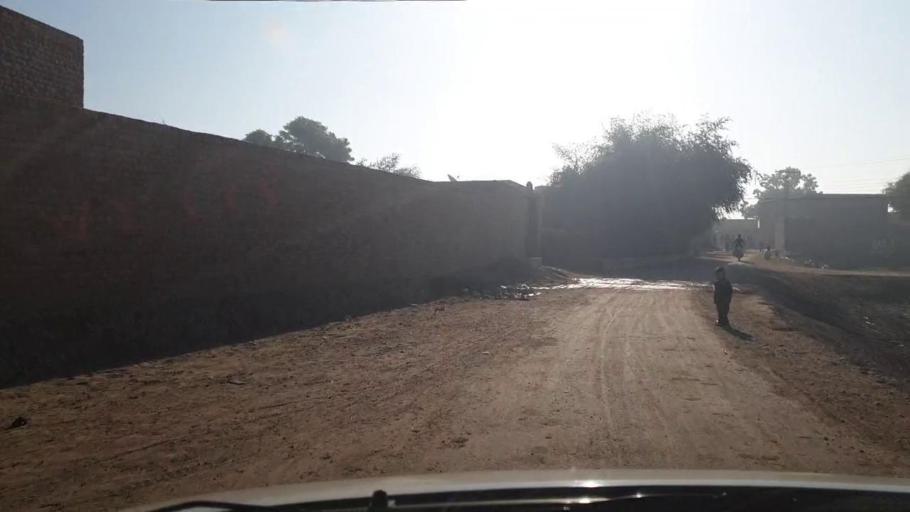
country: PK
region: Sindh
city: Dadu
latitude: 26.6828
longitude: 67.7800
